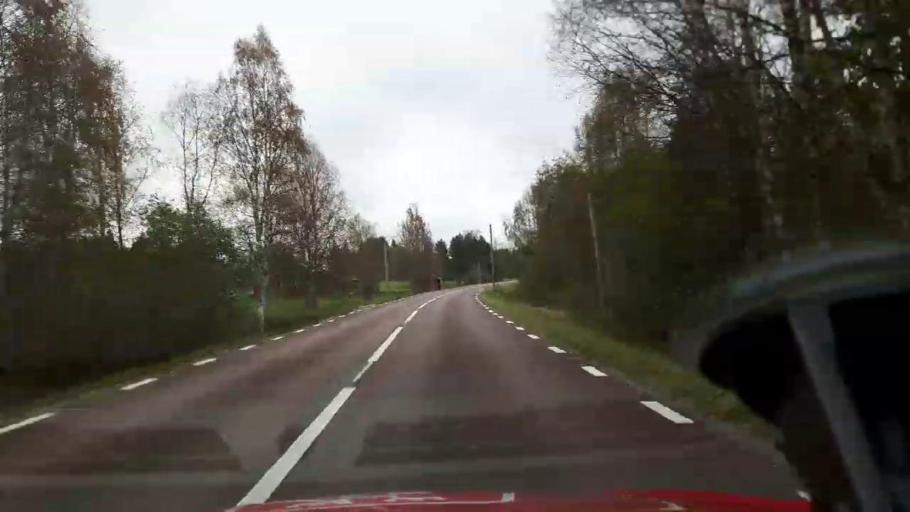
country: SE
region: Jaemtland
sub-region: Harjedalens Kommun
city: Sveg
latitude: 62.3092
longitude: 14.7619
